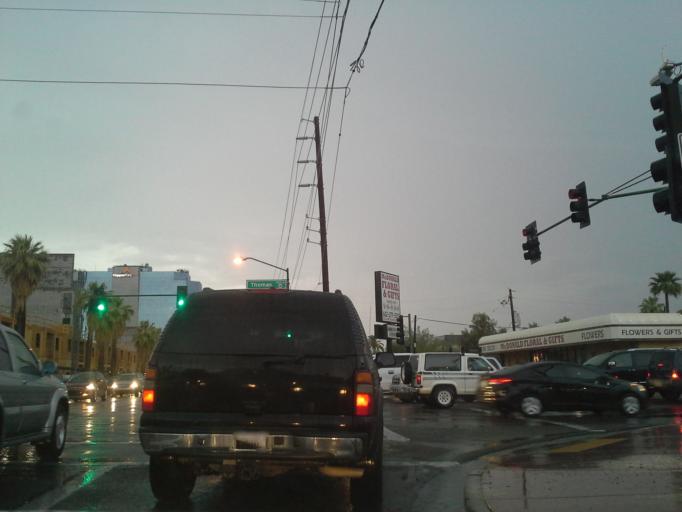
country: US
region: Arizona
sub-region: Maricopa County
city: Phoenix
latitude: 33.4800
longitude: -112.0694
